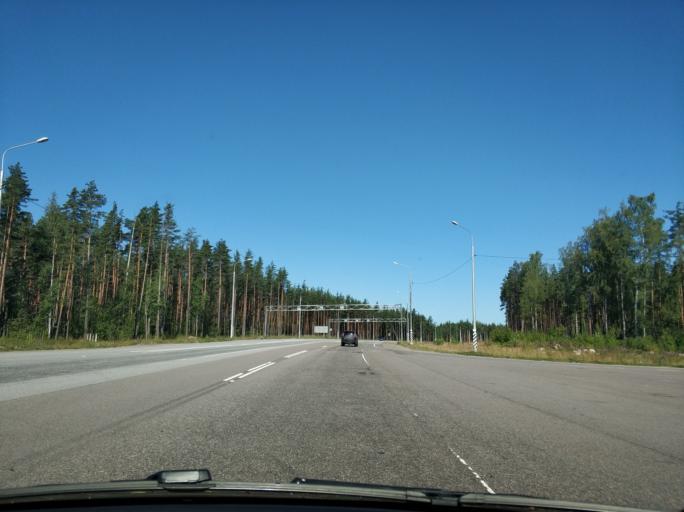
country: RU
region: Leningrad
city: Sapernoye
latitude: 60.6842
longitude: 29.9821
